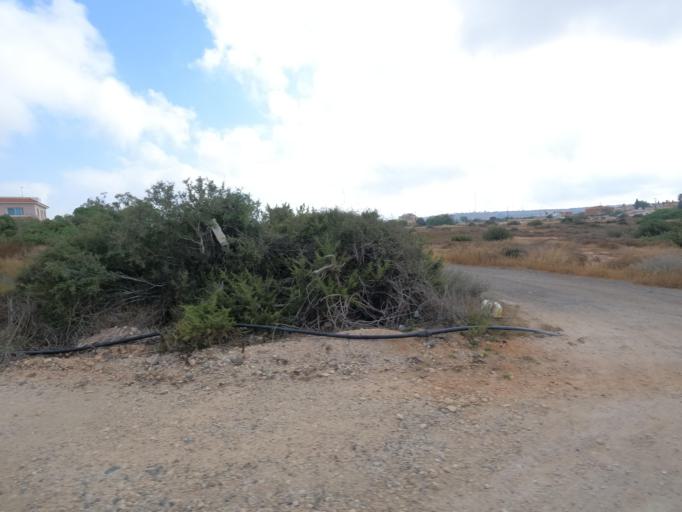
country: CY
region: Ammochostos
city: Ayia Napa
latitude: 35.0025
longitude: 34.0104
